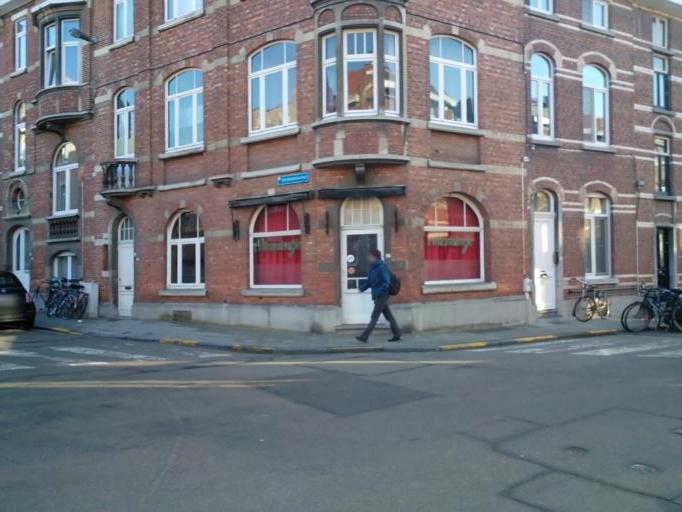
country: BE
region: Flanders
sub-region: Provincie Vlaams-Brabant
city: Leuven
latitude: 50.8698
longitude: 4.7051
